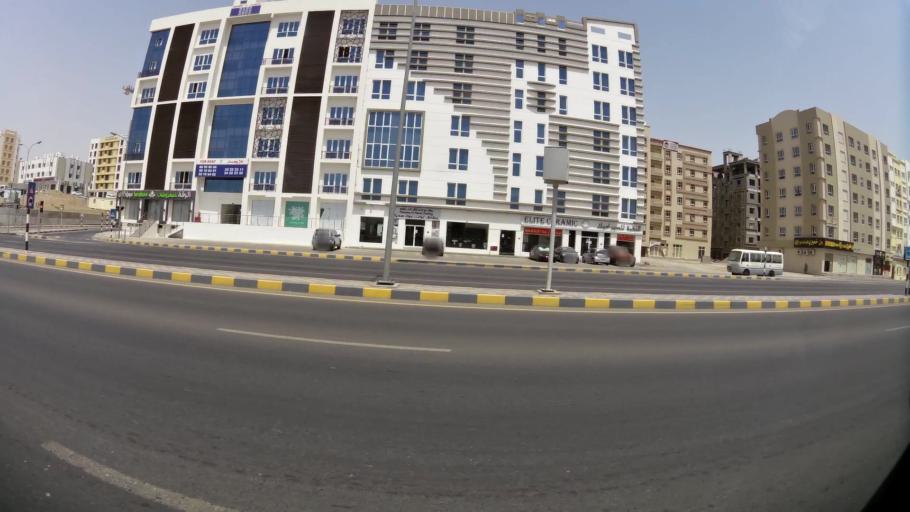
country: OM
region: Muhafazat Masqat
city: Bawshar
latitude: 23.5608
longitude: 58.4023
